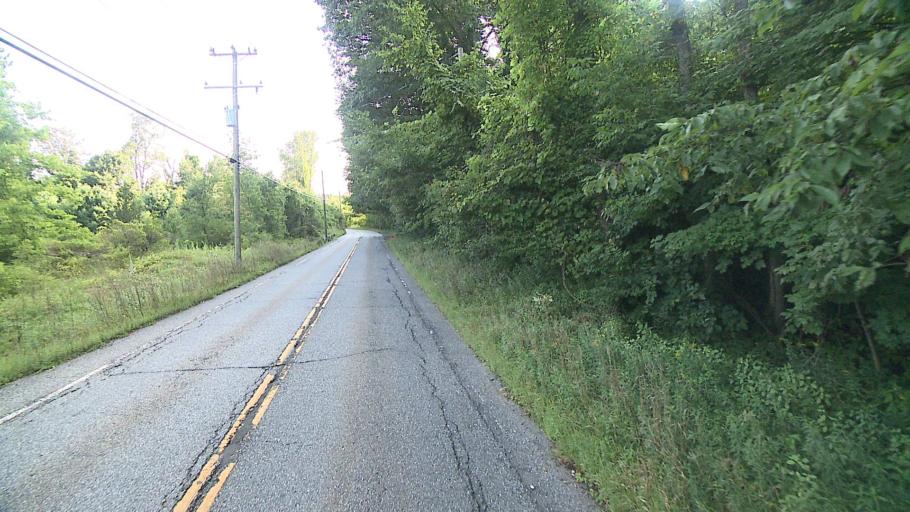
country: US
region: Connecticut
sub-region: Litchfield County
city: Kent
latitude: 41.7987
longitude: -73.3913
